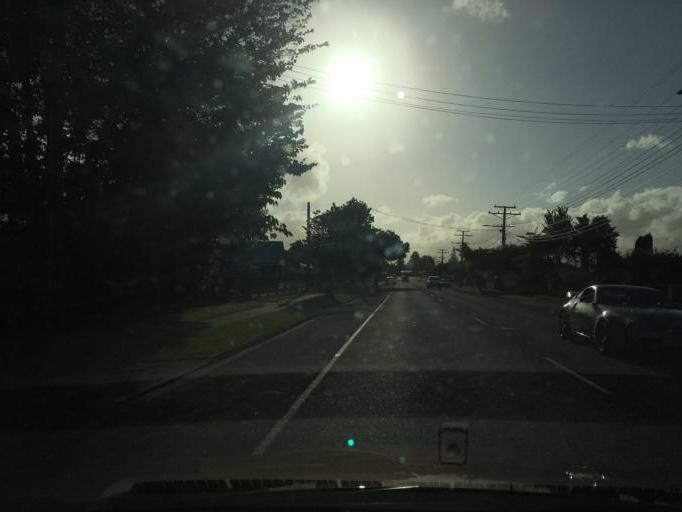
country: NZ
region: Waikato
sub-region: Waipa District
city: Cambridge
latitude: -38.0072
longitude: 175.3345
